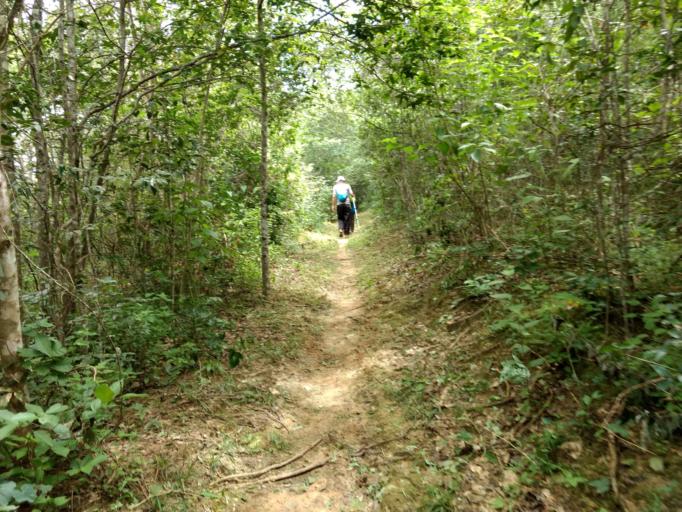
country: BR
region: Ceara
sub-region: Crateus
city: Crateus
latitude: -5.1575
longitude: -40.8976
